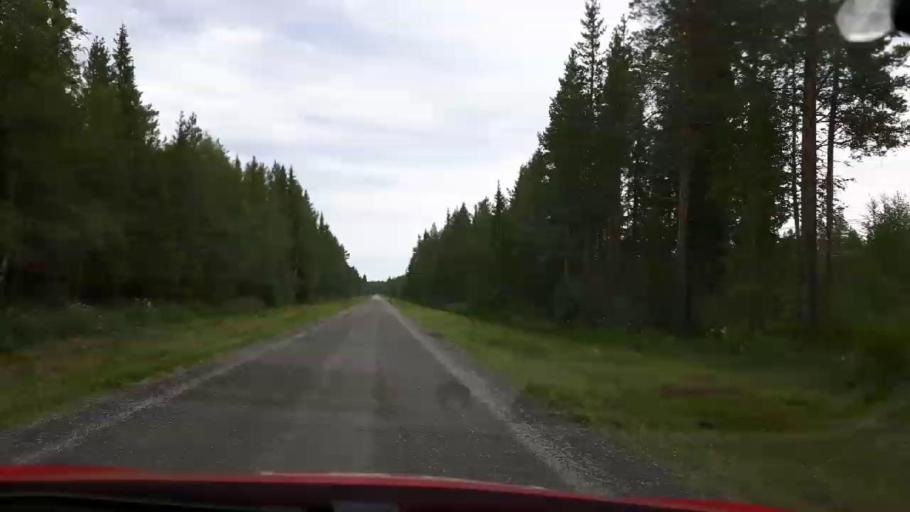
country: SE
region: Jaemtland
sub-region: Stroemsunds Kommun
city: Stroemsund
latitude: 63.7314
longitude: 15.5513
